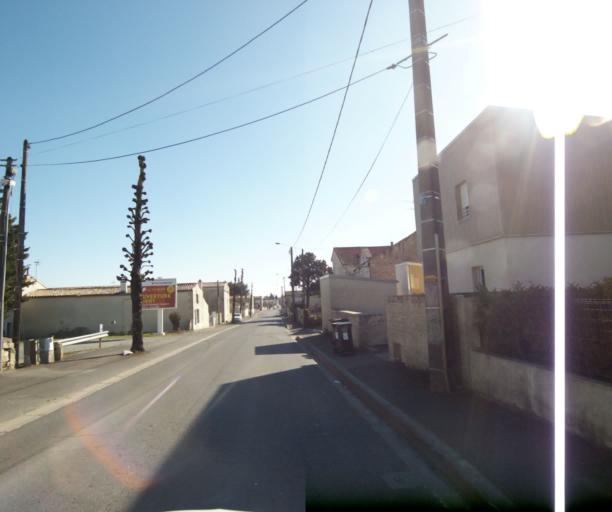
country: FR
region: Poitou-Charentes
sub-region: Departement des Deux-Sevres
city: Niort
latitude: 46.3520
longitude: -0.4789
